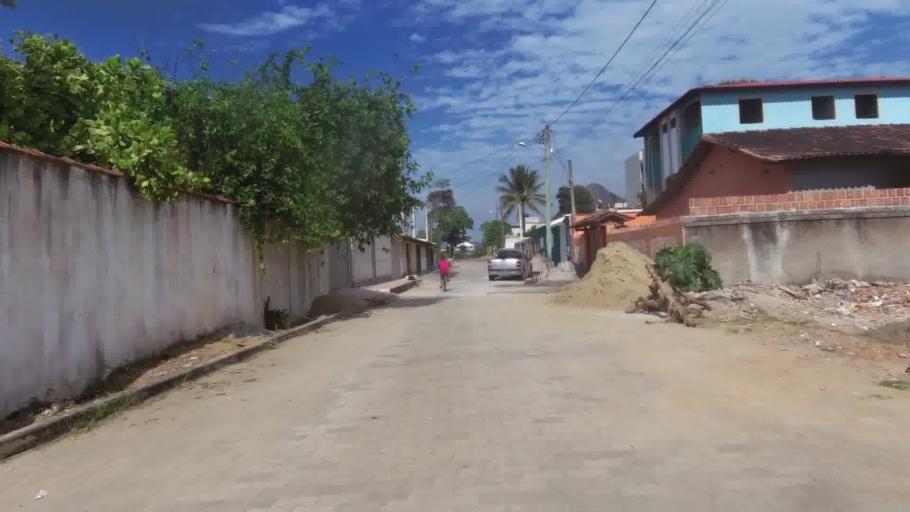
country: BR
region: Espirito Santo
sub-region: Piuma
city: Piuma
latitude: -20.8522
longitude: -40.7497
